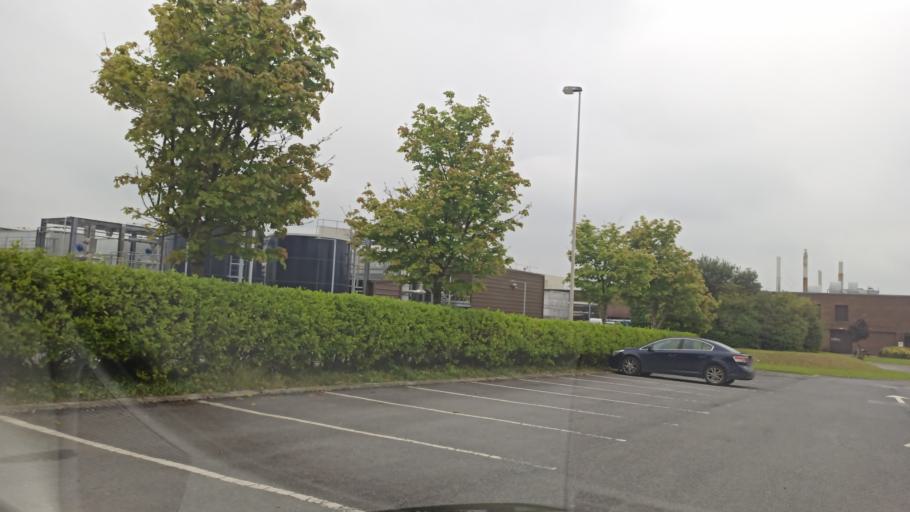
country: IE
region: Munster
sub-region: South Tipperary
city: Cluain Meala
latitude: 52.3725
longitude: -7.7250
